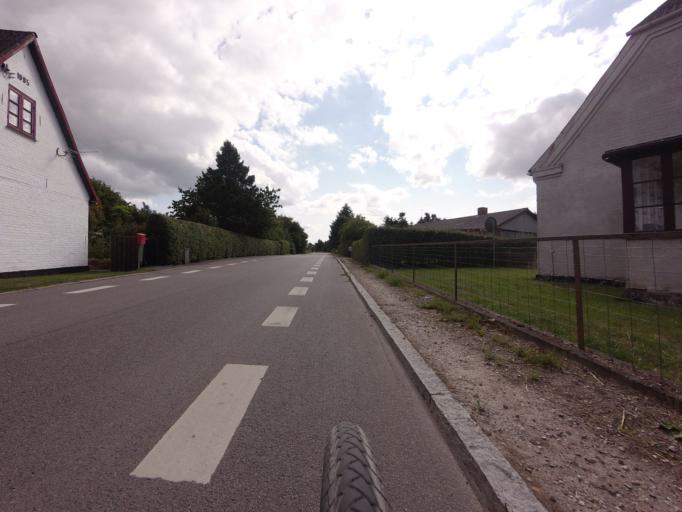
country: DK
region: Zealand
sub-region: Vordingborg Kommune
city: Stege
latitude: 55.0002
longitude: 12.3131
